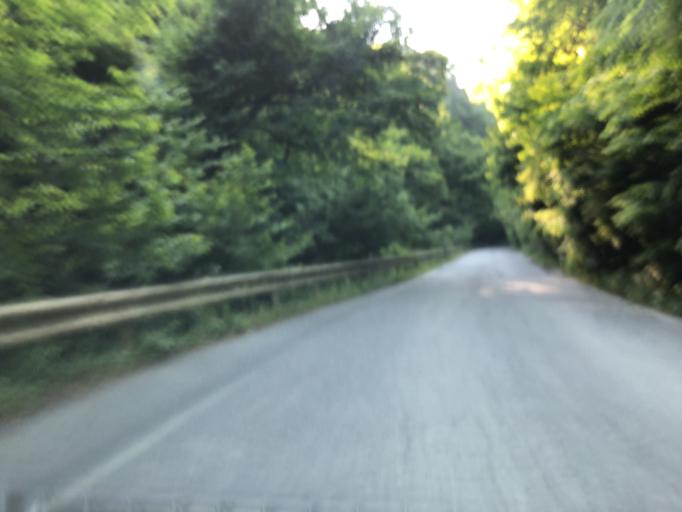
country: JP
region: Ibaraki
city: Kitaibaraki
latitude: 36.8662
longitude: 140.7071
